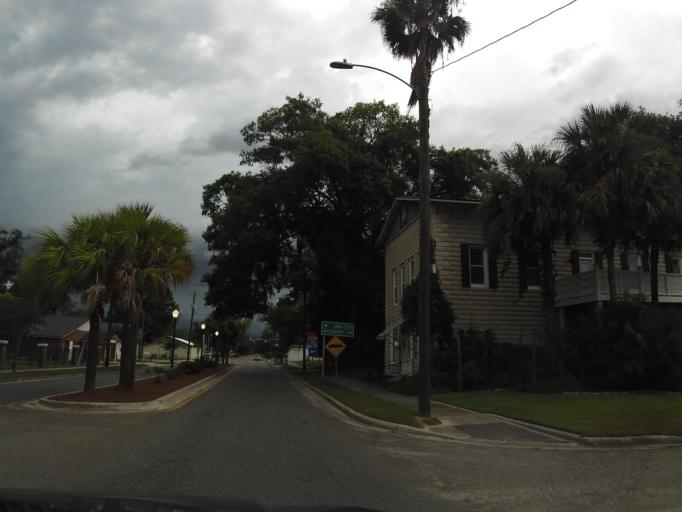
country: US
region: Florida
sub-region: Baker County
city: Macclenny
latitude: 30.2752
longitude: -82.1607
